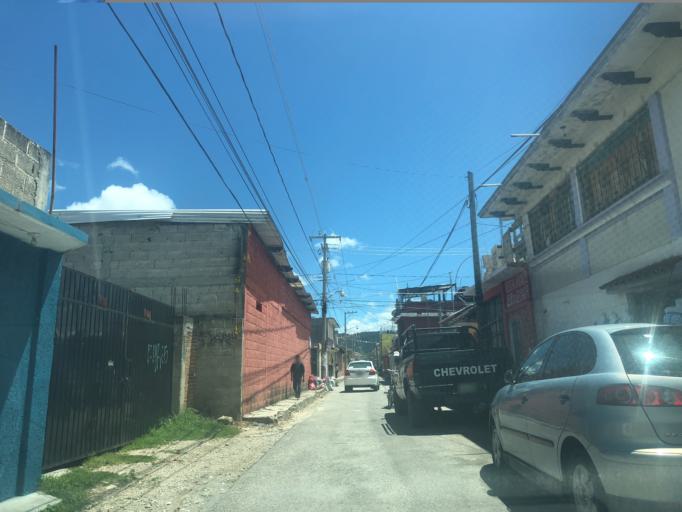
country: MX
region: Chiapas
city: San Cristobal de las Casas
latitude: 16.7176
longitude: -92.6438
